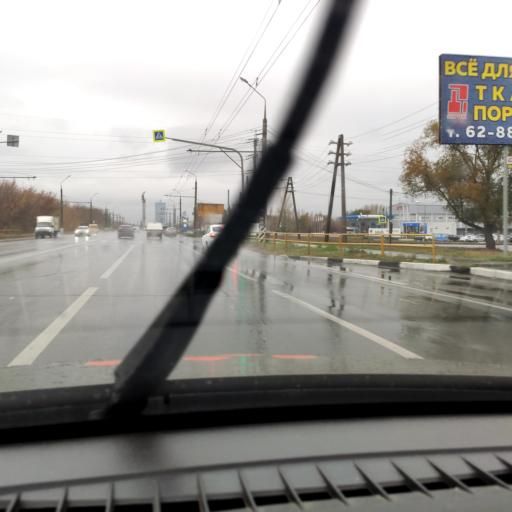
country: RU
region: Samara
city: Tol'yatti
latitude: 53.5528
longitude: 49.2943
